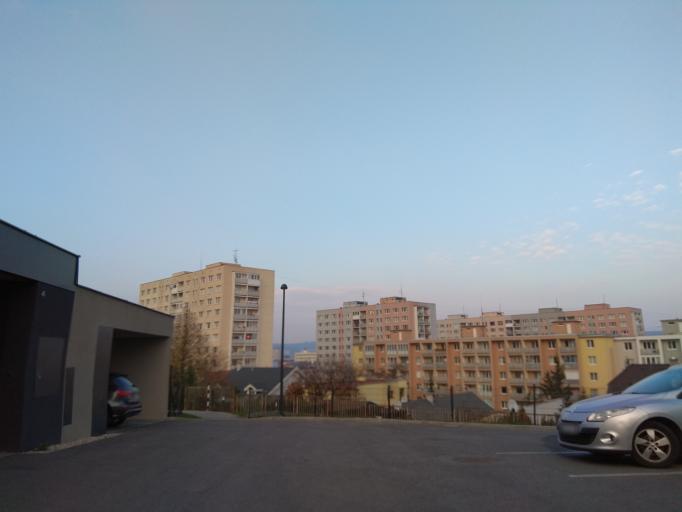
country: SK
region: Kosicky
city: Kosice
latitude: 48.7252
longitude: 21.2402
